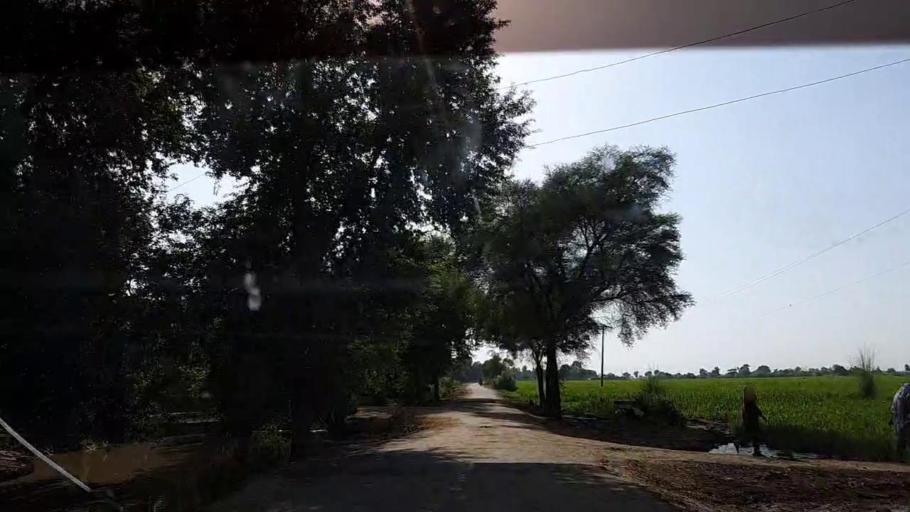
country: PK
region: Sindh
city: Tangwani
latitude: 28.2153
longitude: 68.9826
